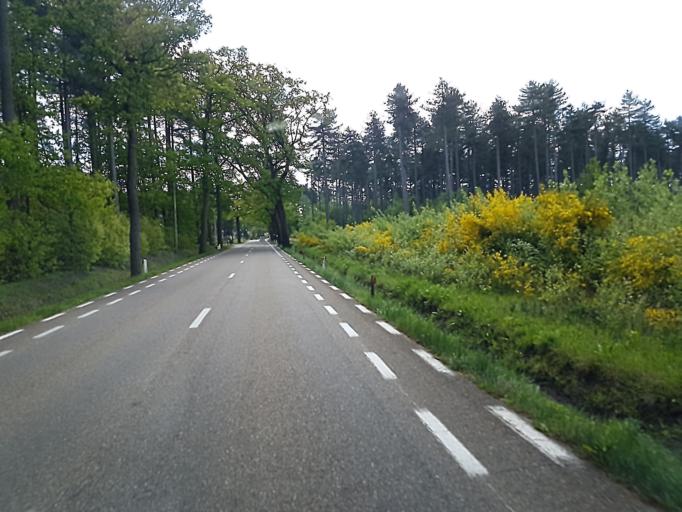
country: BE
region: Flanders
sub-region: Provincie Antwerpen
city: Laakdal
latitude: 51.0419
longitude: 5.0078
